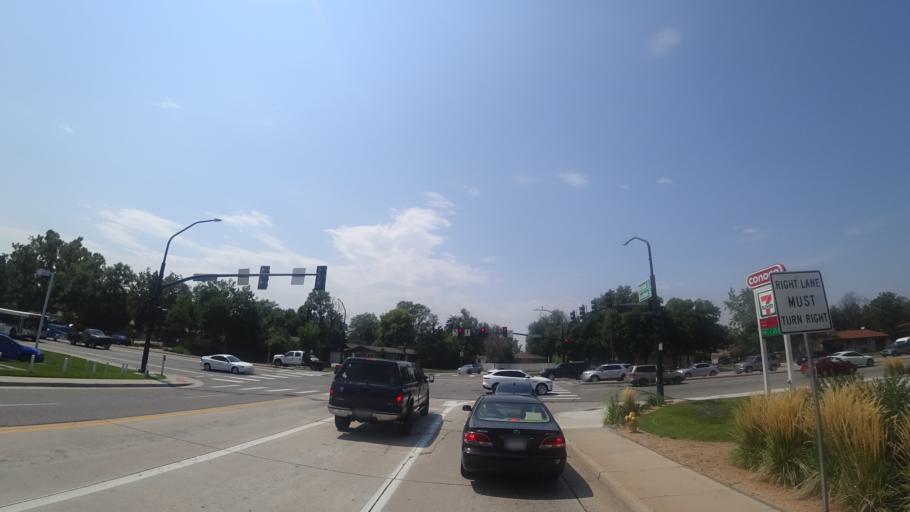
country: US
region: Colorado
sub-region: Arapahoe County
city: Littleton
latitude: 39.6096
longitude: -104.9876
